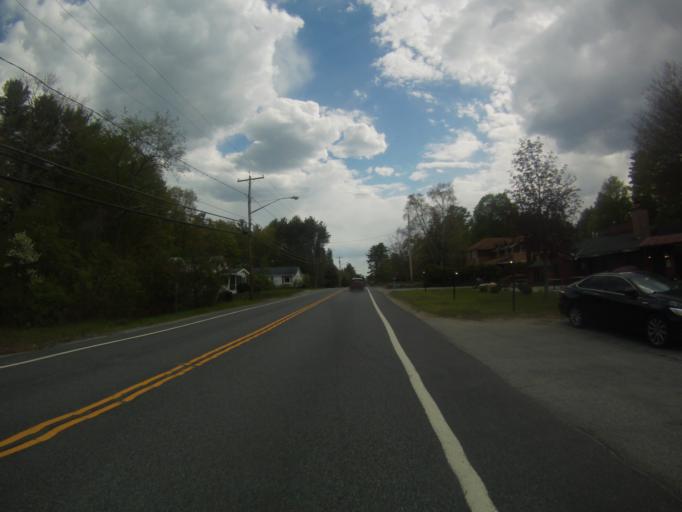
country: US
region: New York
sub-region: Essex County
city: Ticonderoga
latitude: 43.8515
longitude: -73.7572
